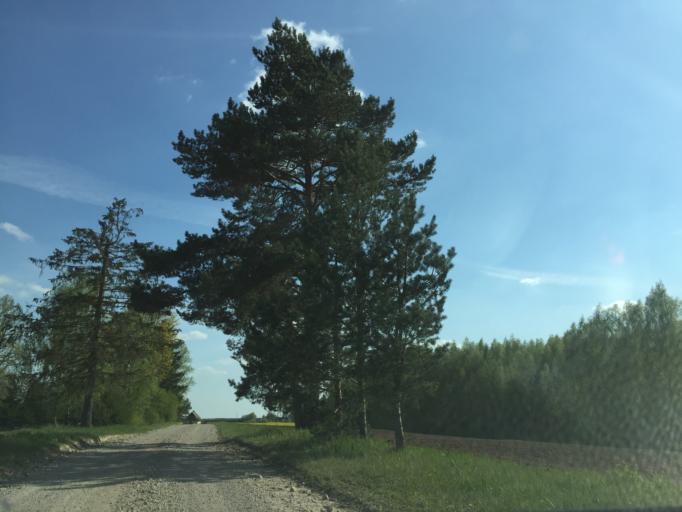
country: LV
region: Lecava
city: Iecava
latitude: 56.5013
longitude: 24.3183
